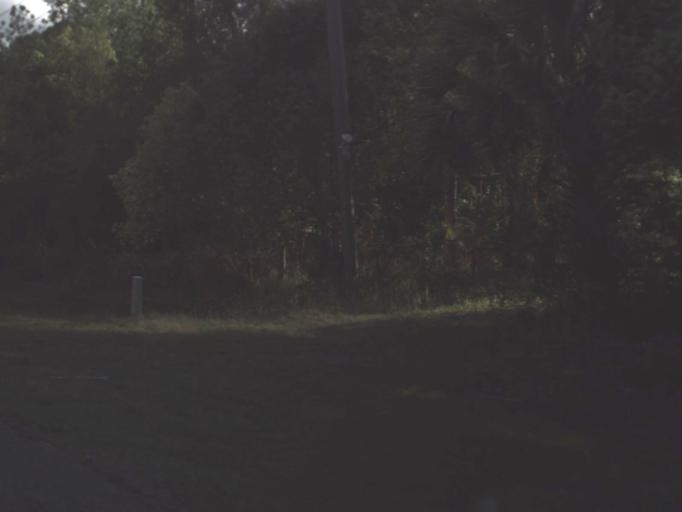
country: US
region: Florida
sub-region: Flagler County
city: Bunnell
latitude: 29.3361
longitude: -81.3108
